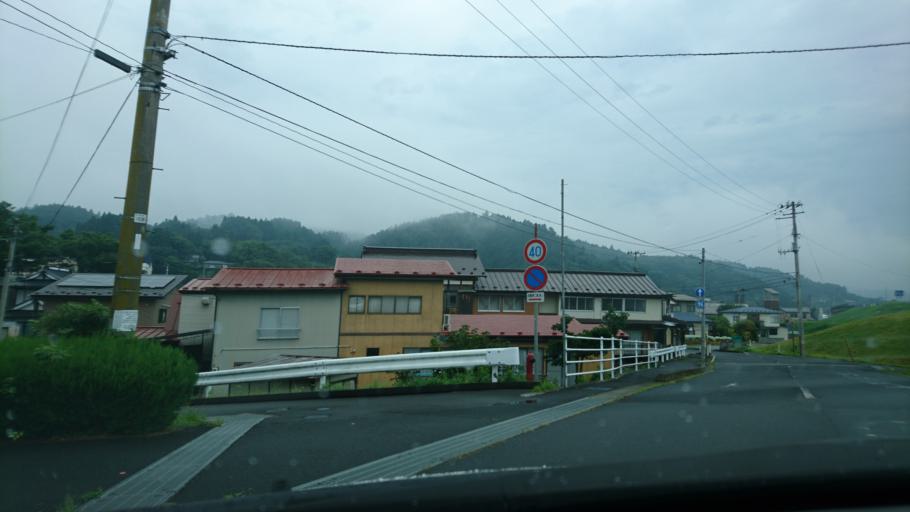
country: JP
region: Iwate
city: Ichinoseki
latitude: 38.8998
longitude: 141.2634
